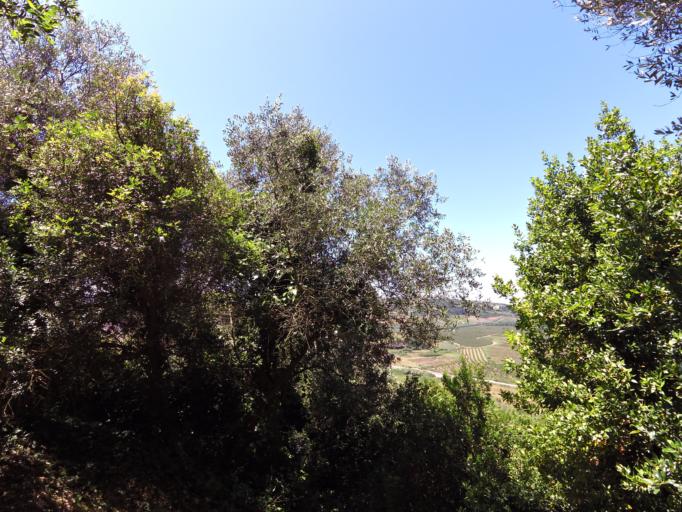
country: PT
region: Leiria
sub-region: Obidos
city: Obidos
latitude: 39.3623
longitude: -9.1580
